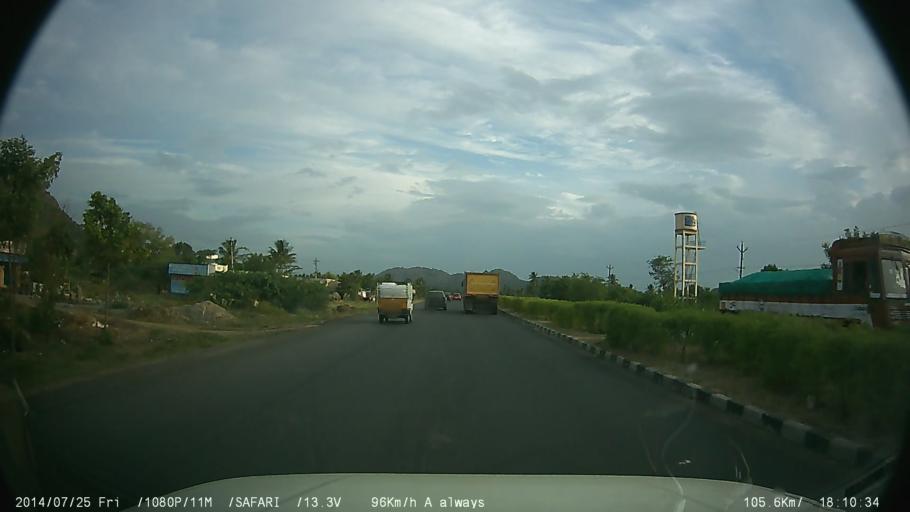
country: IN
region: Tamil Nadu
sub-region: Krishnagiri
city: Kaverippattanam
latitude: 12.3737
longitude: 78.2167
